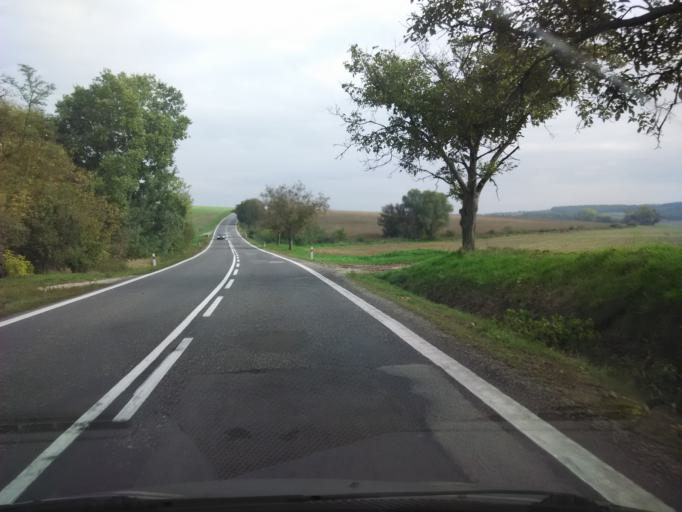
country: SK
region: Nitriansky
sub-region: Okres Nitra
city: Vrable
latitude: 48.2755
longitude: 18.2327
